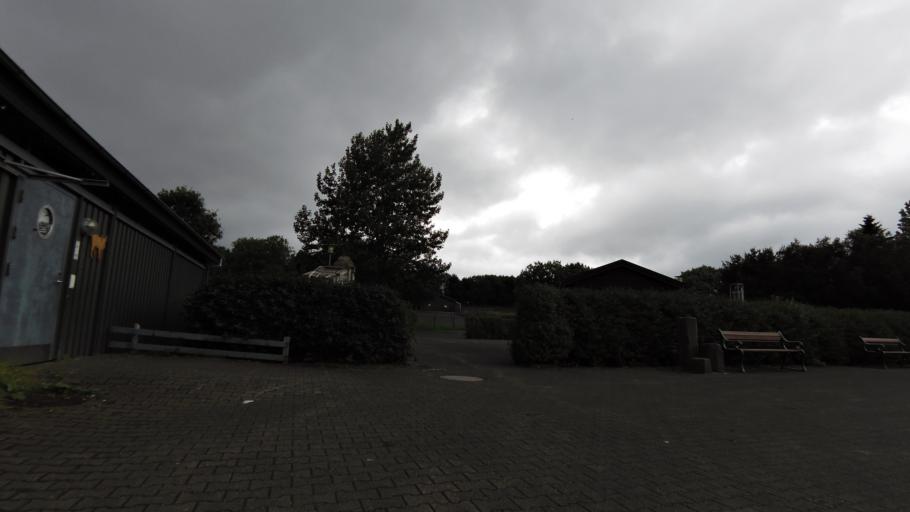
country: IS
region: Capital Region
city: Reykjavik
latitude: 64.1391
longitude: -21.8714
